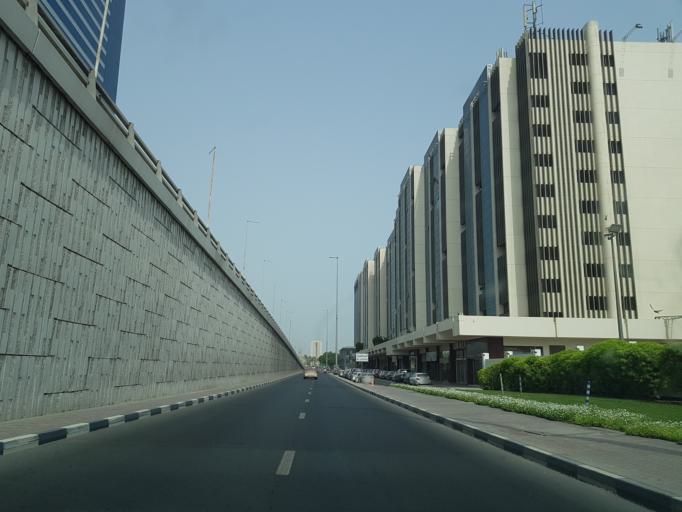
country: AE
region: Ash Shariqah
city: Sharjah
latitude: 25.2306
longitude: 55.2881
